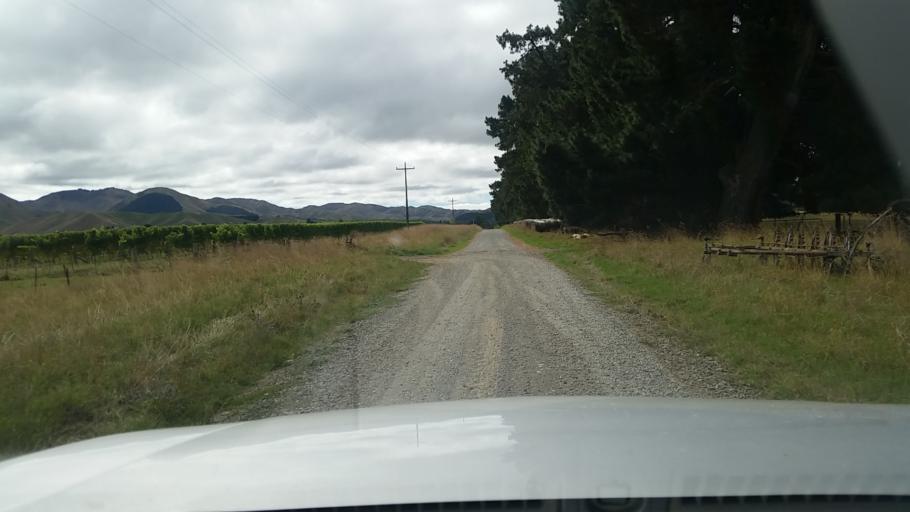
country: NZ
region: Marlborough
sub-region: Marlborough District
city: Blenheim
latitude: -41.6758
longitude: 174.0386
